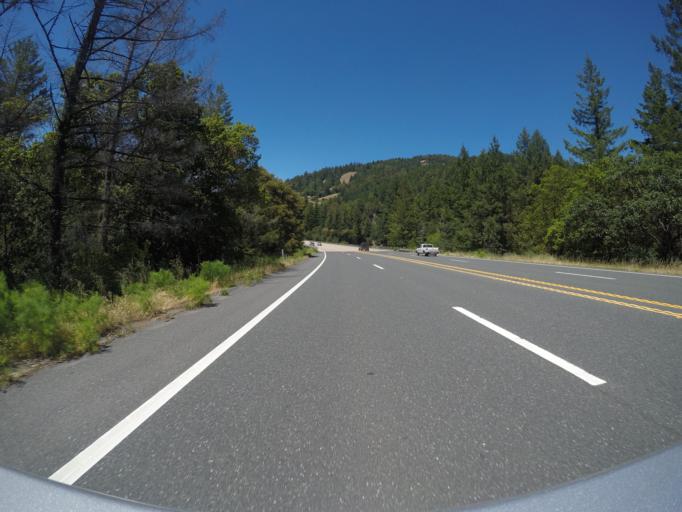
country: US
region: California
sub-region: Humboldt County
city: Redway
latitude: 39.9547
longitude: -123.7800
